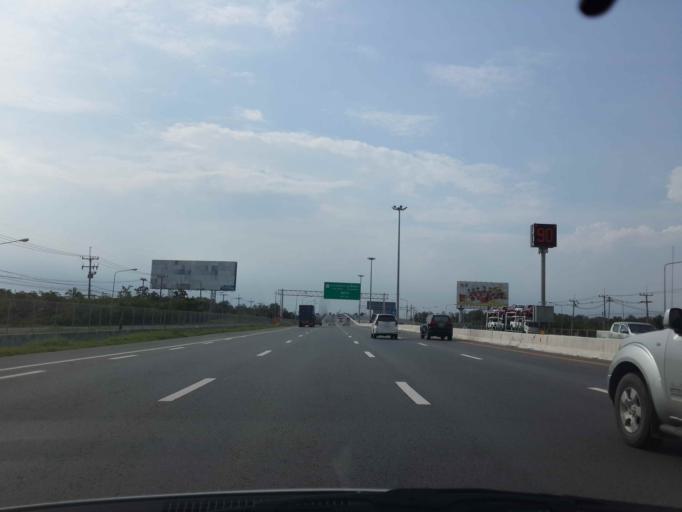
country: TH
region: Chachoengsao
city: Bang Pakong
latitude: 13.5441
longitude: 101.0047
